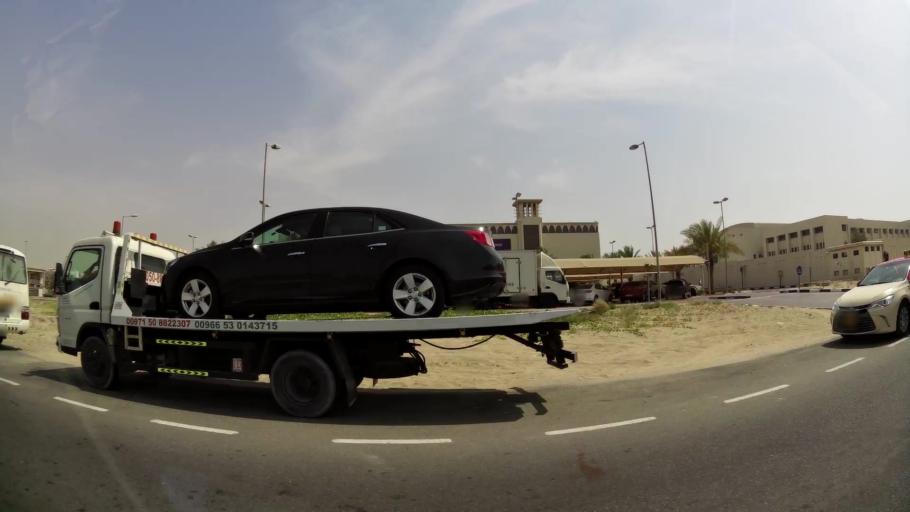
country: AE
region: Ash Shariqah
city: Sharjah
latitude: 25.2510
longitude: 55.4538
